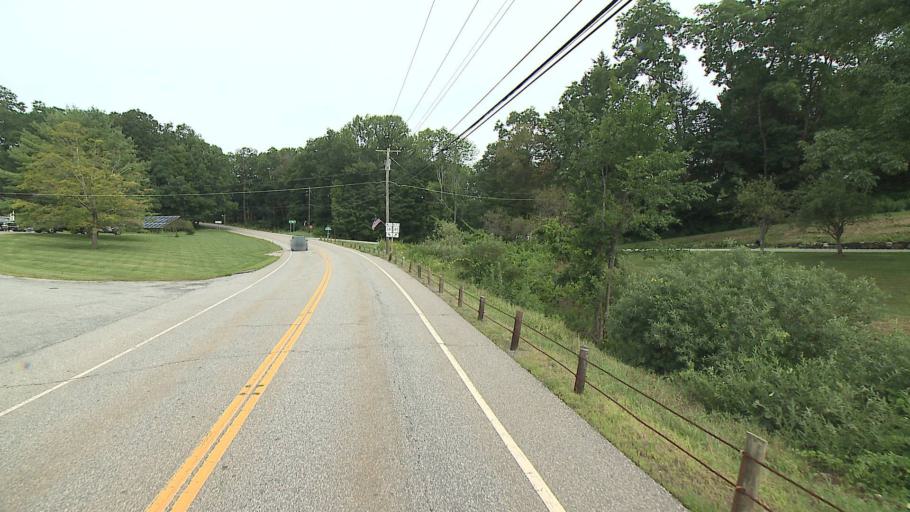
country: US
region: Connecticut
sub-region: Litchfield County
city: New Preston
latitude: 41.7438
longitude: -73.3452
